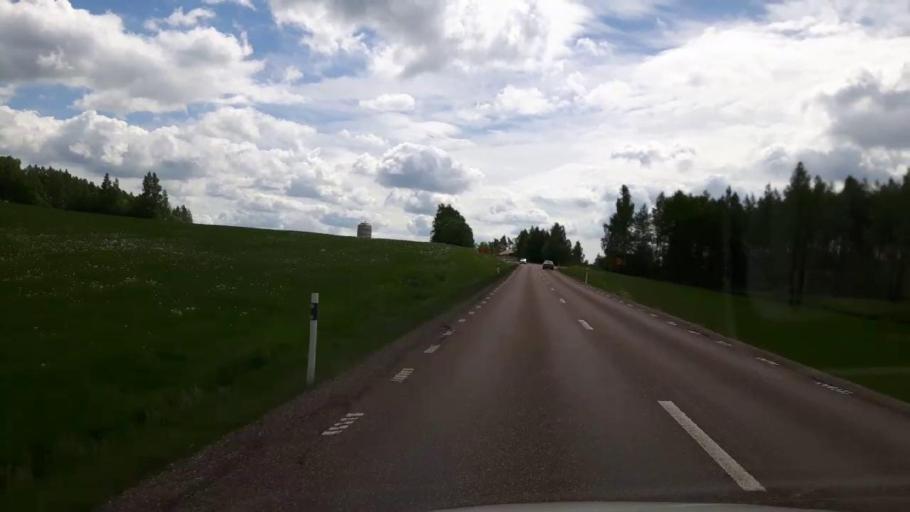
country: SE
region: Dalarna
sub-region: Saters Kommun
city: Saeter
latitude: 60.4309
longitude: 15.8317
